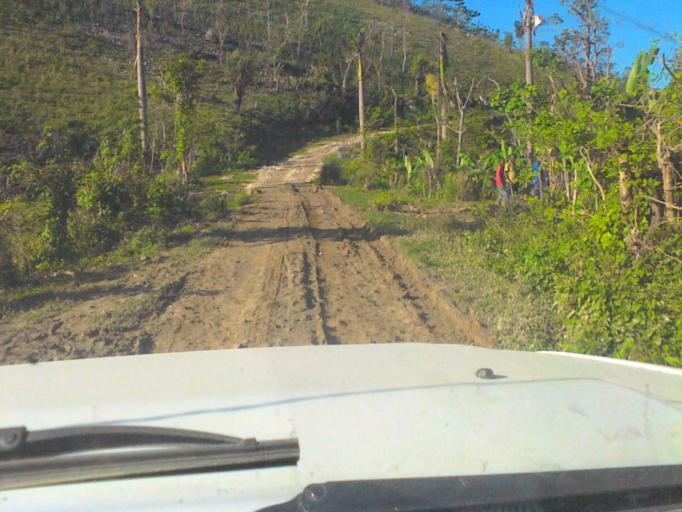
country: HT
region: Grandans
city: Jeremie
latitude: 18.5129
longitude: -74.0834
